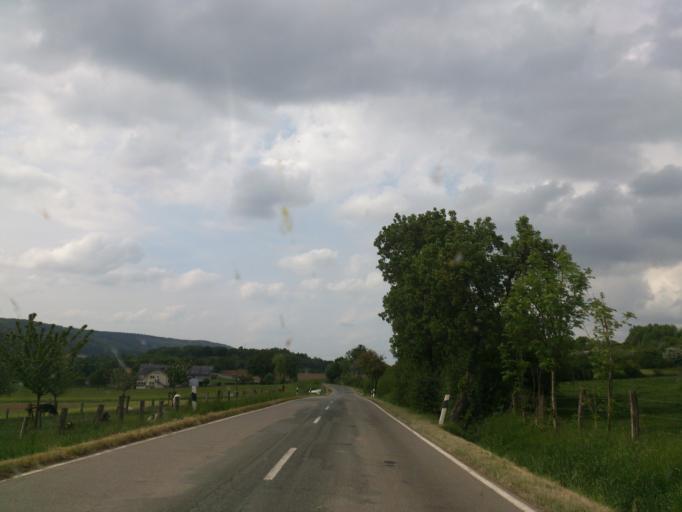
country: DE
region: North Rhine-Westphalia
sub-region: Regierungsbezirk Detmold
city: Willebadessen
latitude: 51.5662
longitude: 9.0500
